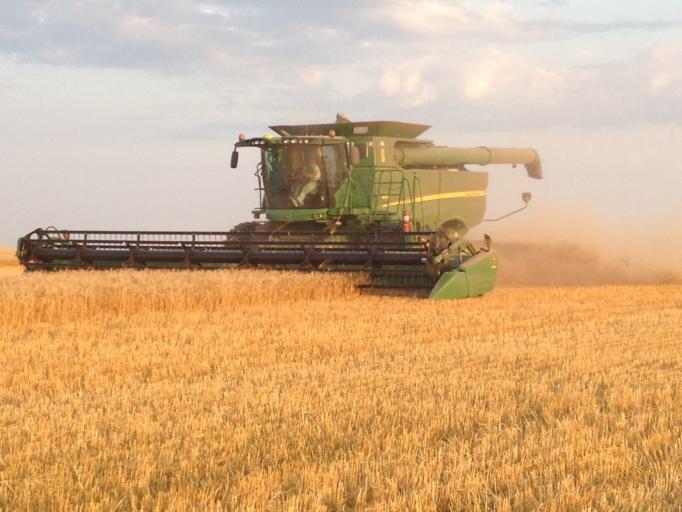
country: US
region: North Dakota
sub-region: Hettinger County
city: Mott
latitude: 46.3977
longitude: -102.5495
